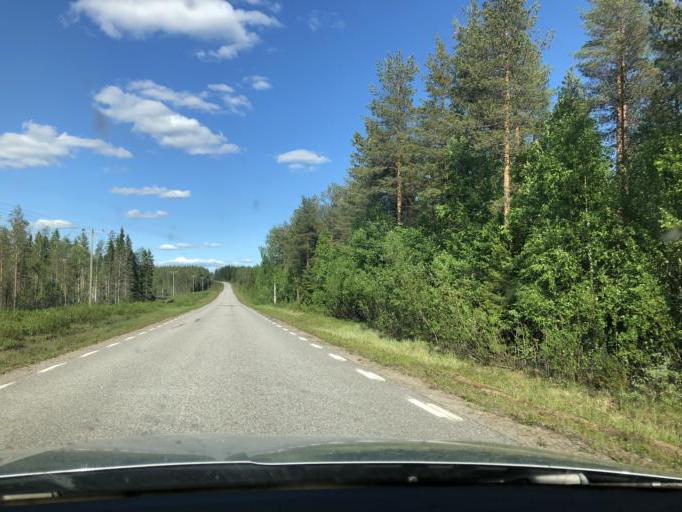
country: SE
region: Norrbotten
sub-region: Kalix Kommun
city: Kalix
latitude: 66.0940
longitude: 23.2555
